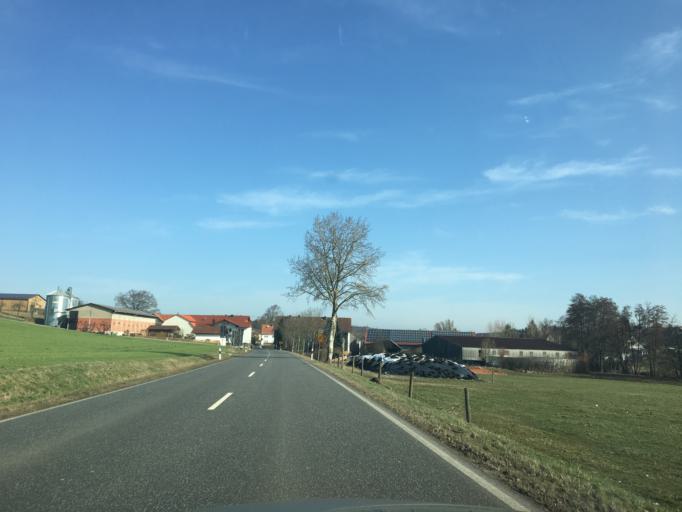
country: DE
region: Hesse
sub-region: Regierungsbezirk Giessen
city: Schwalmtal
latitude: 50.6609
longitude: 9.2705
